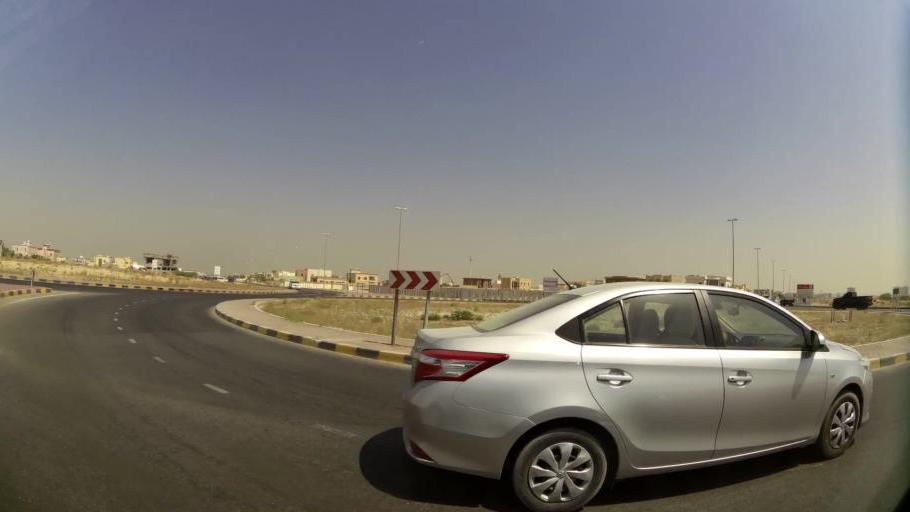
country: AE
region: Ajman
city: Ajman
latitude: 25.4129
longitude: 55.5277
